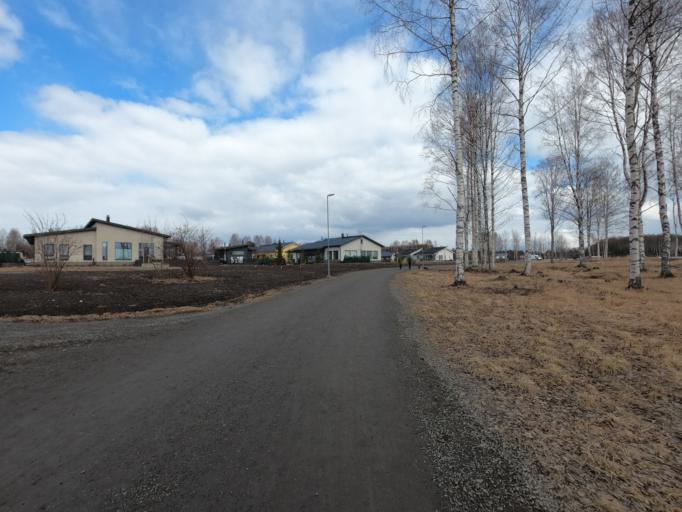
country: FI
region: North Karelia
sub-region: Joensuu
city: Joensuu
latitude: 62.6148
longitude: 29.8559
